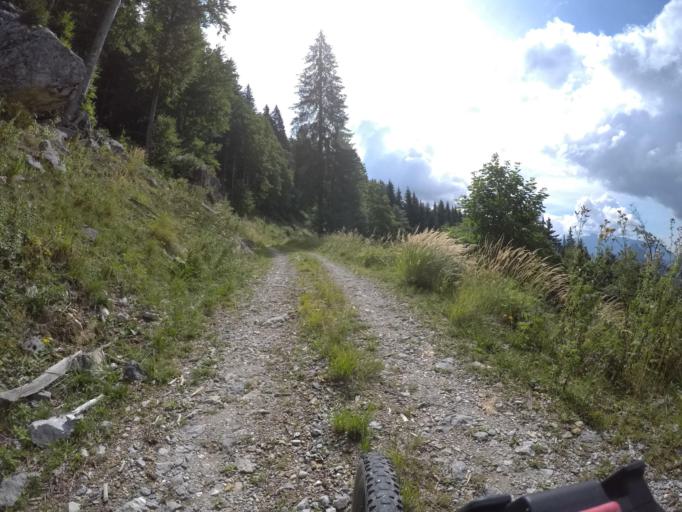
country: IT
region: Friuli Venezia Giulia
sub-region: Provincia di Udine
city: Paularo
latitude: 46.5128
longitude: 13.1955
